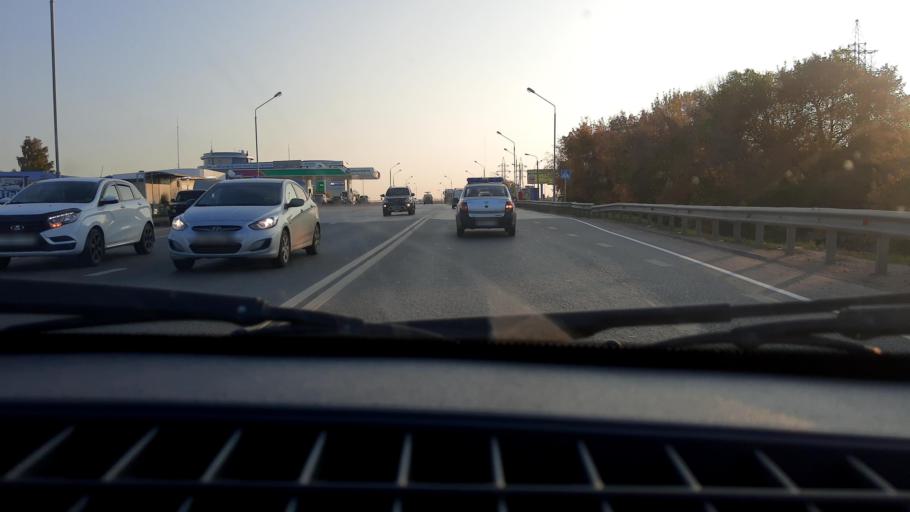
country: RU
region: Bashkortostan
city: Avdon
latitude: 54.6799
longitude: 55.8063
